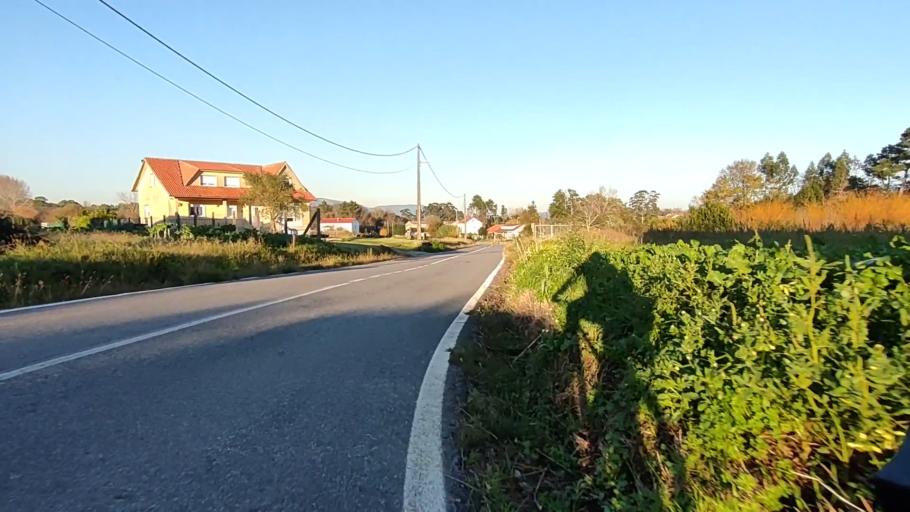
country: ES
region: Galicia
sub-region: Provincia da Coruna
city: Rianxo
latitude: 42.6347
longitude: -8.8579
